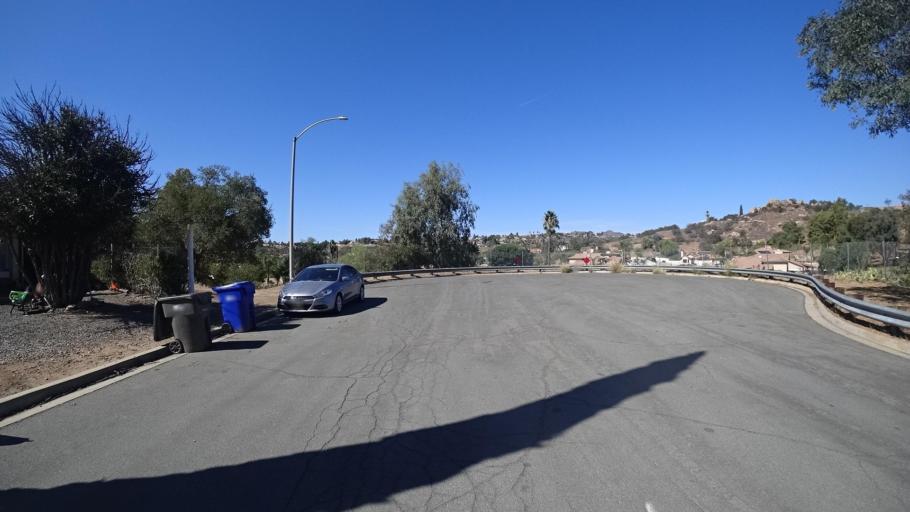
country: US
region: California
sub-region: San Diego County
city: Crest
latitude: 32.8497
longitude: -116.8648
